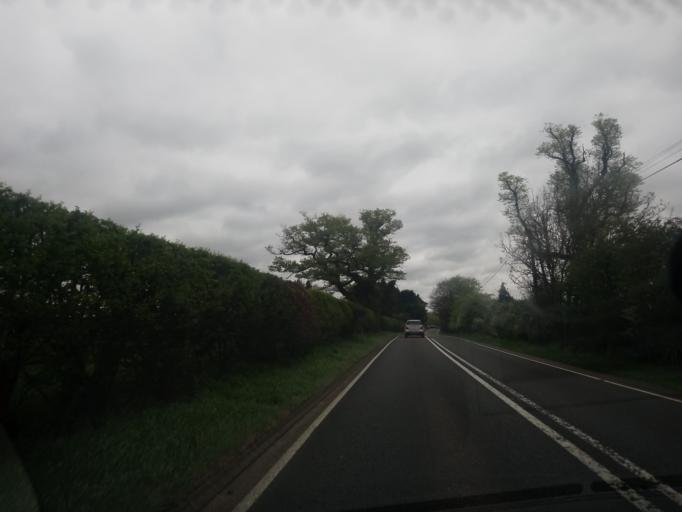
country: GB
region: England
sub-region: Telford and Wrekin
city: Chetwynd
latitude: 52.8059
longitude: -2.4339
